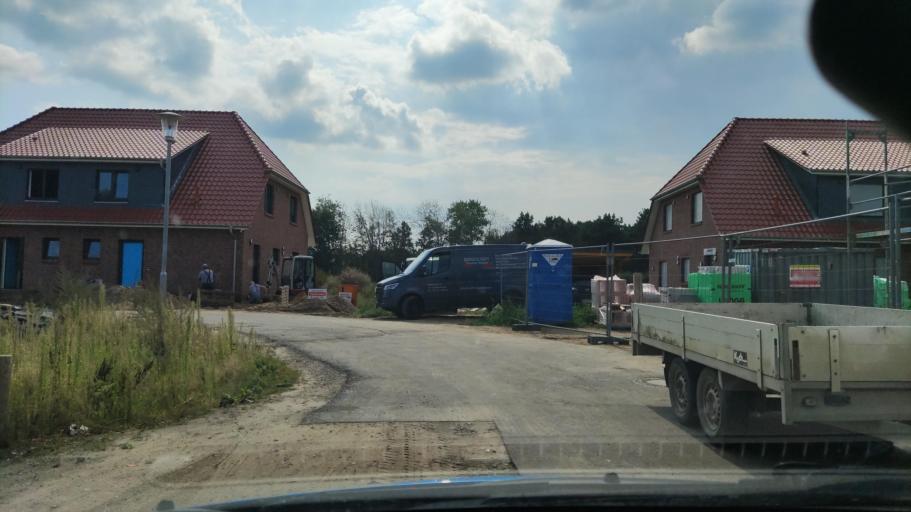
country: DE
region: Lower Saxony
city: Barum
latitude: 53.3430
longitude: 10.4121
